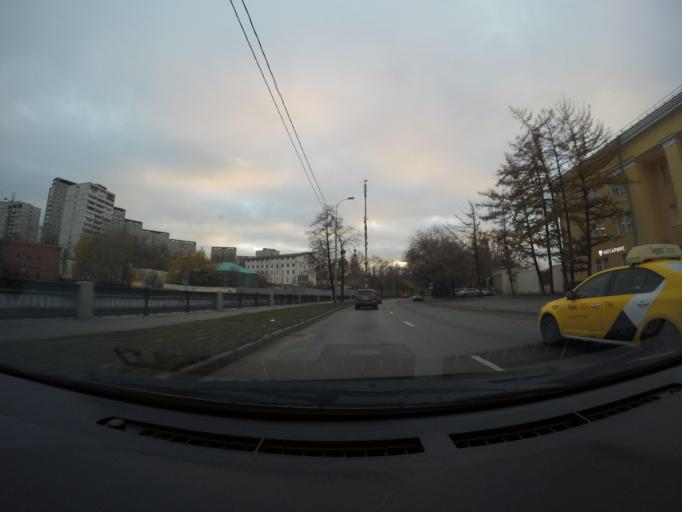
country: RU
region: Moscow
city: Lefortovo
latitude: 55.7604
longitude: 37.6835
